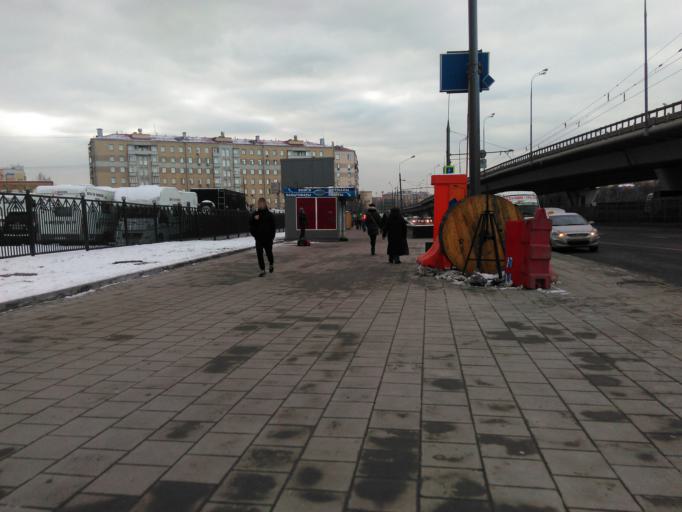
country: RU
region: Moscow
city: Rostokino
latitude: 55.8226
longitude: 37.6439
